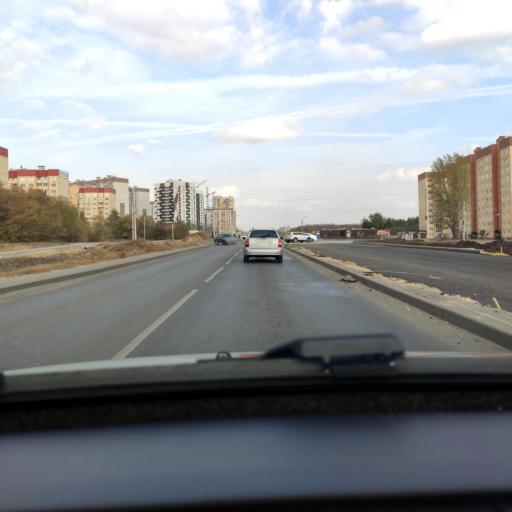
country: RU
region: Voronezj
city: Shilovo
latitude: 51.5618
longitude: 39.1145
